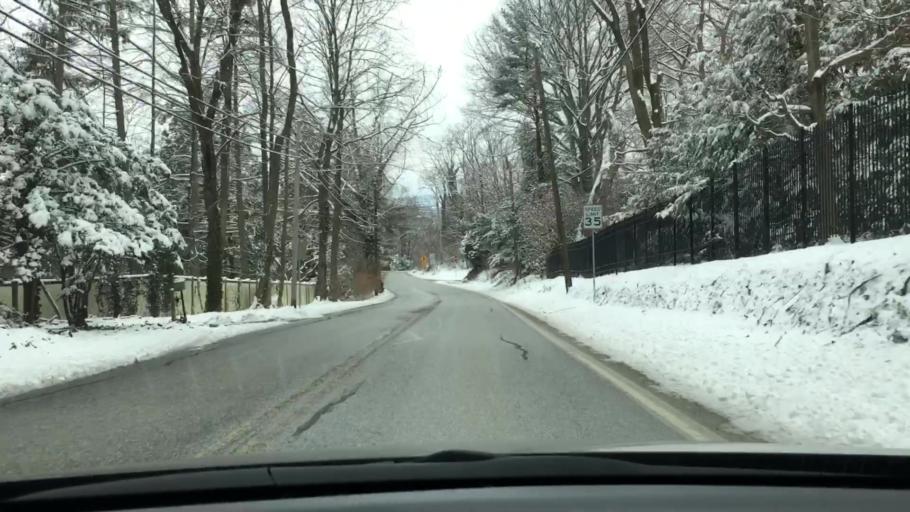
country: US
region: Pennsylvania
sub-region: York County
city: Grantley
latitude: 39.9410
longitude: -76.7304
